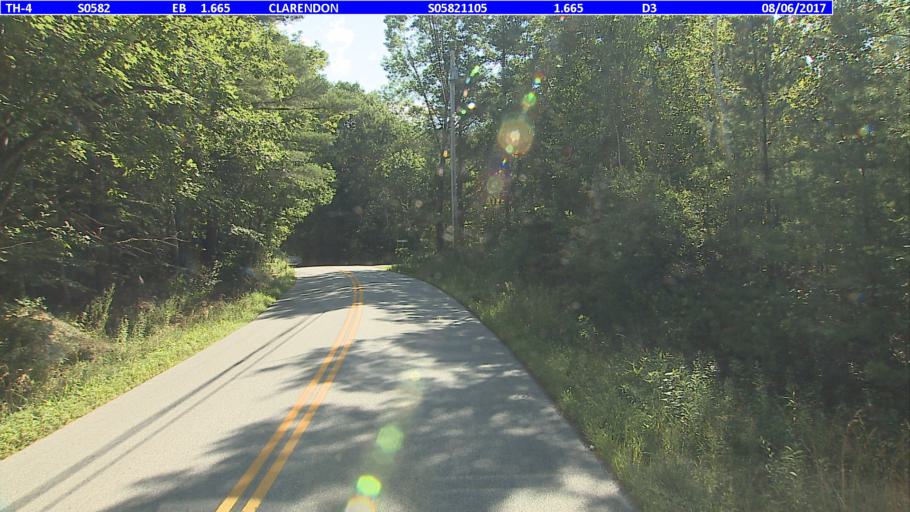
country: US
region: Vermont
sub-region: Rutland County
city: Rutland
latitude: 43.5613
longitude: -72.9363
